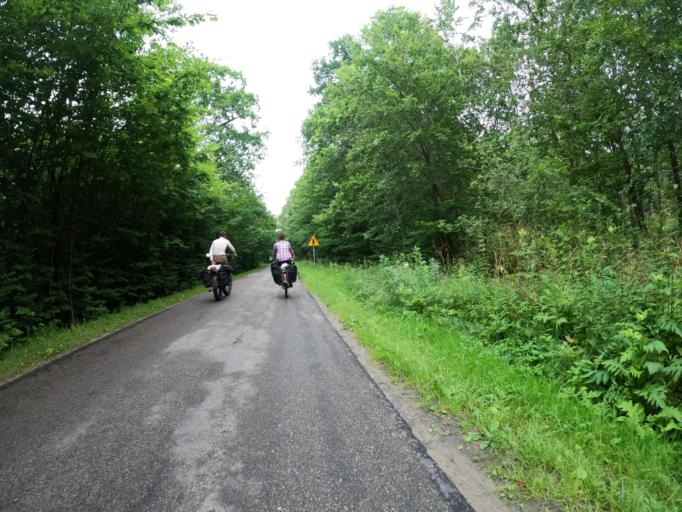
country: PL
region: West Pomeranian Voivodeship
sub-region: Powiat koszalinski
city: Bobolice
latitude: 53.9085
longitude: 16.5079
